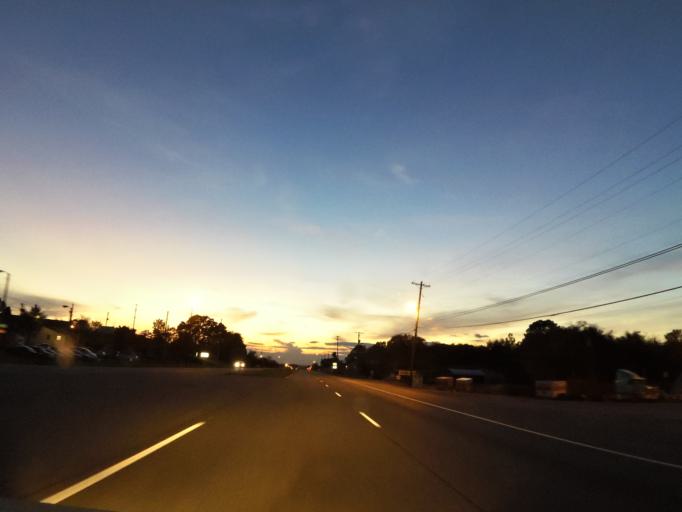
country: US
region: Tennessee
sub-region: Knox County
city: Mascot
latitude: 36.0202
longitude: -83.7908
